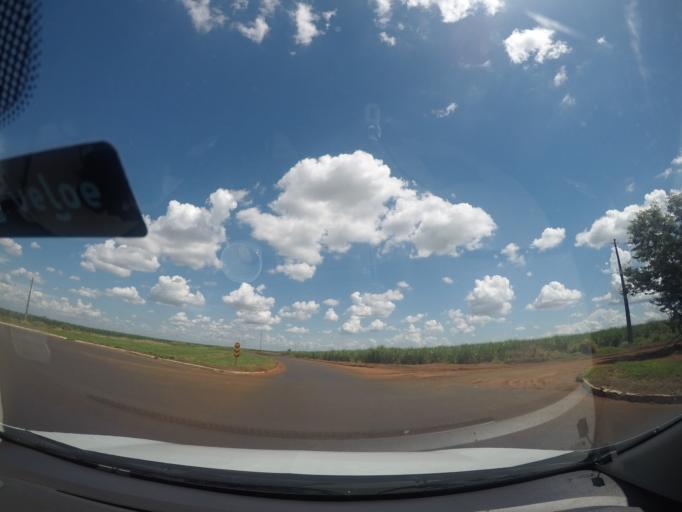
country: BR
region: Minas Gerais
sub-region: Frutal
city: Frutal
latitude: -19.8185
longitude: -48.7319
